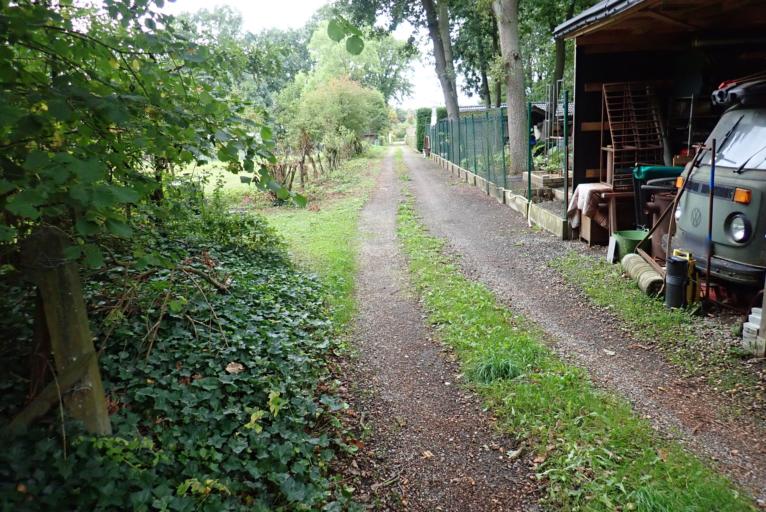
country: BE
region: Flanders
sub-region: Provincie Antwerpen
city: Hulshout
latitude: 51.0668
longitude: 4.7876
